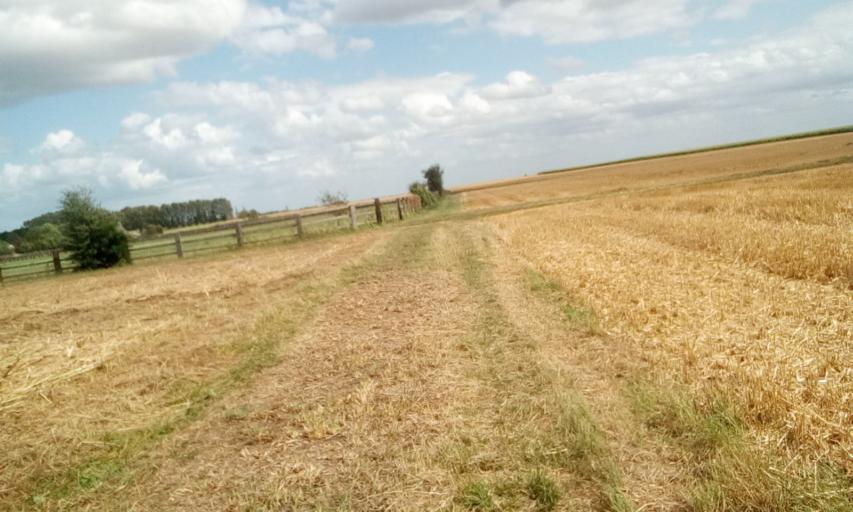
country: FR
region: Lower Normandy
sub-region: Departement du Calvados
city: Creully
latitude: 49.3092
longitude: -0.5551
